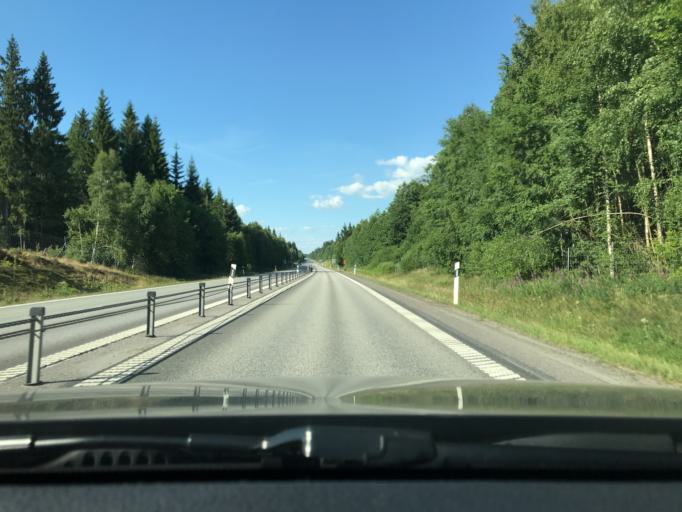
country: SE
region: Skane
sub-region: Osby Kommun
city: Osby
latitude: 56.4119
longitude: 14.0472
